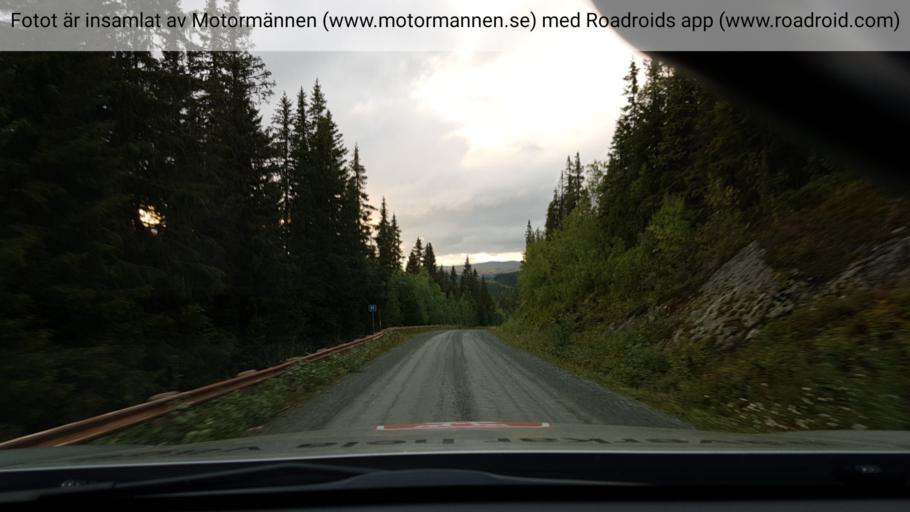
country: SE
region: Vaesterbotten
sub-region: Vilhelmina Kommun
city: Sjoberg
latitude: 65.4964
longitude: 15.4886
